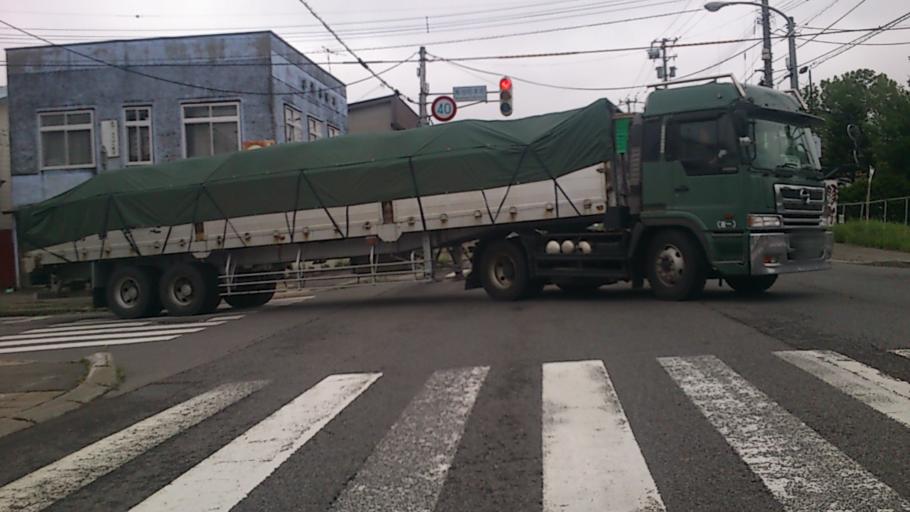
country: JP
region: Hokkaido
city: Obihiro
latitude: 42.9103
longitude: 143.3585
